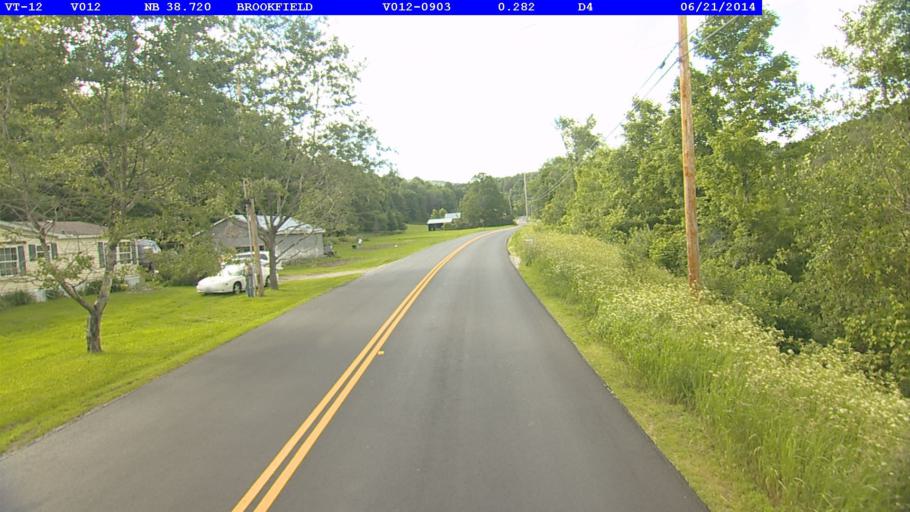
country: US
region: Vermont
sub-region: Orange County
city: Randolph
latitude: 44.0093
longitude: -72.6547
